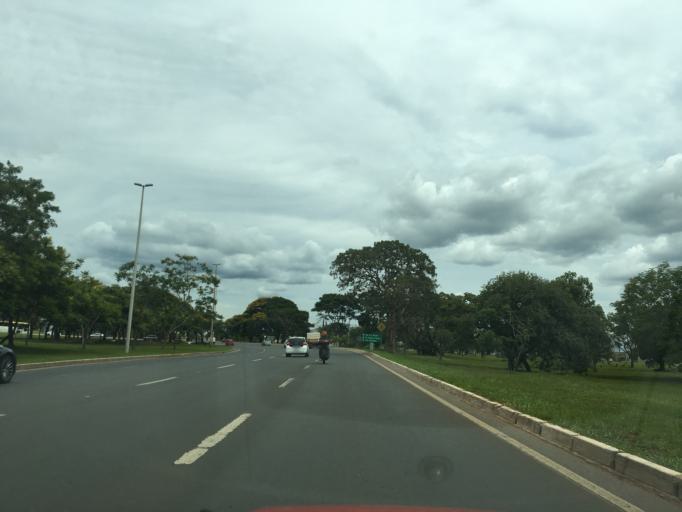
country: BR
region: Federal District
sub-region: Brasilia
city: Brasilia
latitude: -15.7987
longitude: -47.8517
